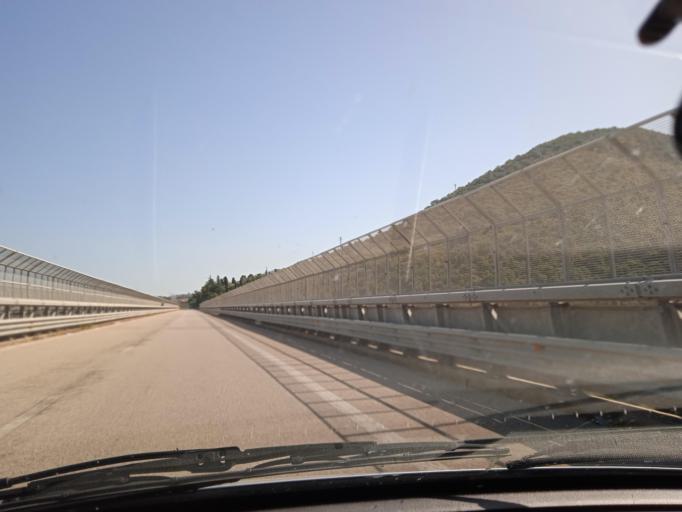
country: IT
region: Sicily
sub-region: Messina
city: Rocca di Capri Leone
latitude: 38.1095
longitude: 14.7224
